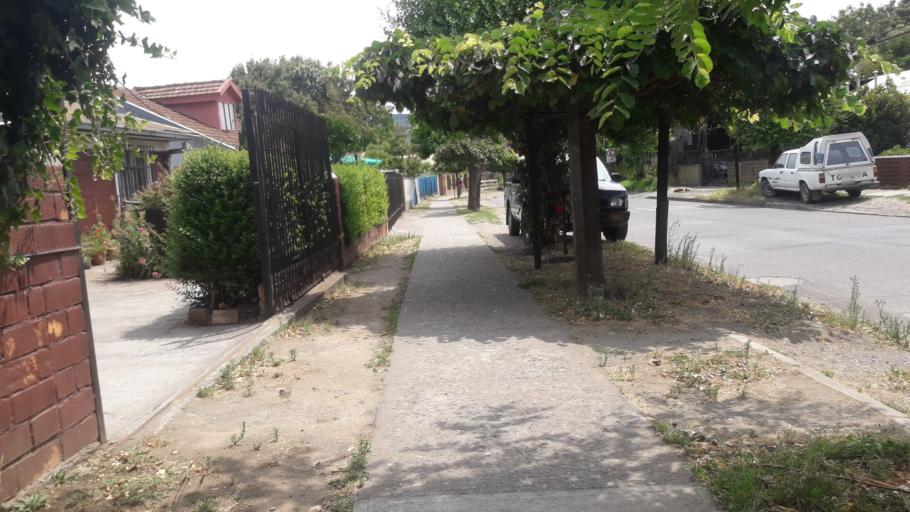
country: CL
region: Biobio
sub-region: Provincia de Biobio
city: Nacimiento
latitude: -37.5047
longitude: -72.6813
